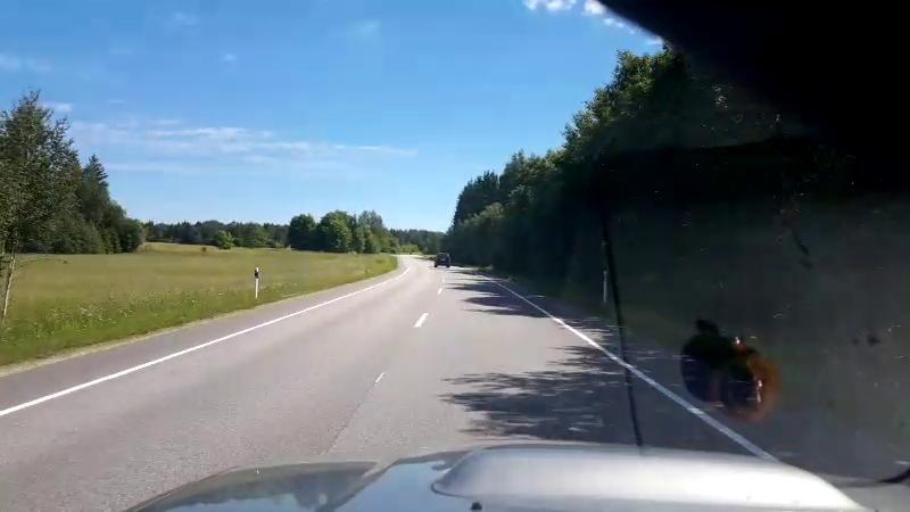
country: EE
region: Jaervamaa
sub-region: Jaerva-Jaani vald
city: Jarva-Jaani
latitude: 59.0165
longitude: 25.9107
